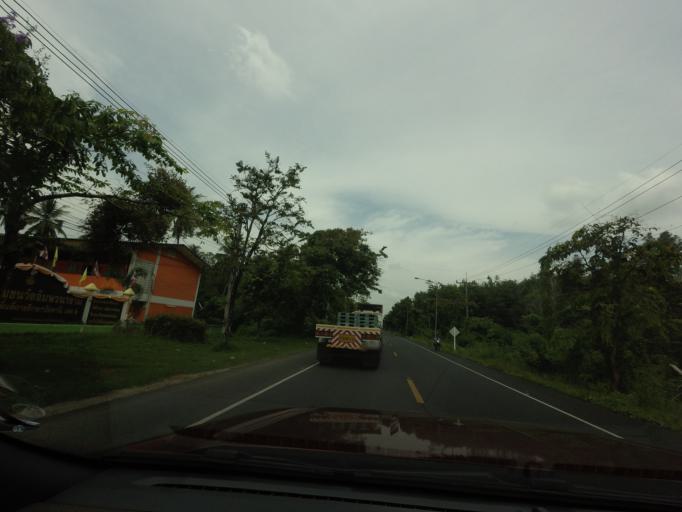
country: TH
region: Pattani
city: Mae Lan
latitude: 6.6521
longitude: 101.3028
